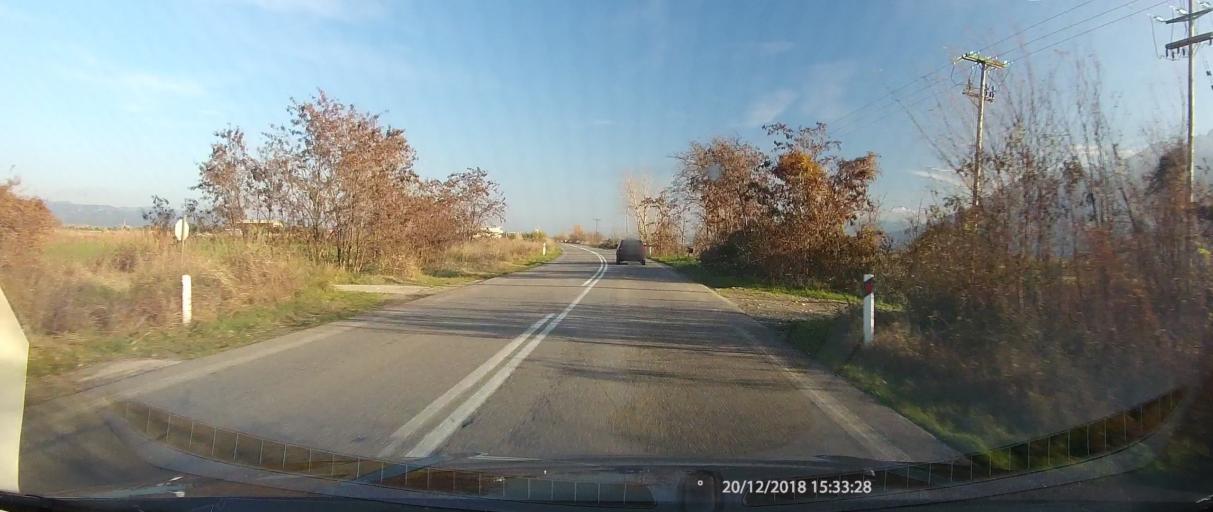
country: GR
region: Central Greece
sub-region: Nomos Fthiotidos
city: Lianokladhion
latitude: 38.9236
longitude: 22.2769
